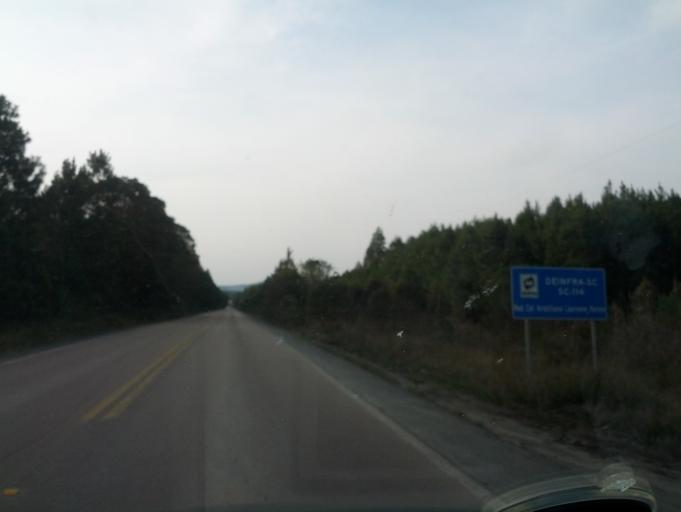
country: BR
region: Santa Catarina
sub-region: Otacilio Costa
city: Otacilio Costa
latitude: -27.3855
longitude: -50.1343
